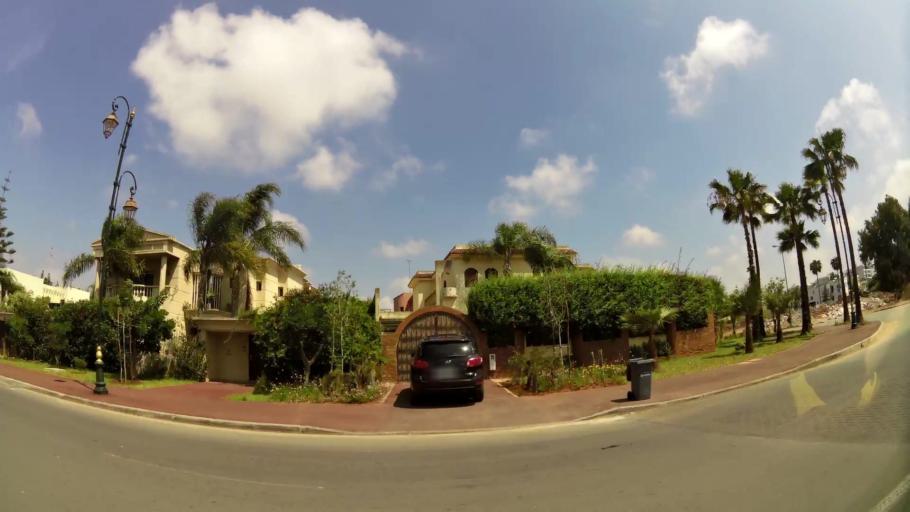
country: MA
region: Rabat-Sale-Zemmour-Zaer
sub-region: Skhirate-Temara
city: Temara
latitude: 33.9603
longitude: -6.8848
